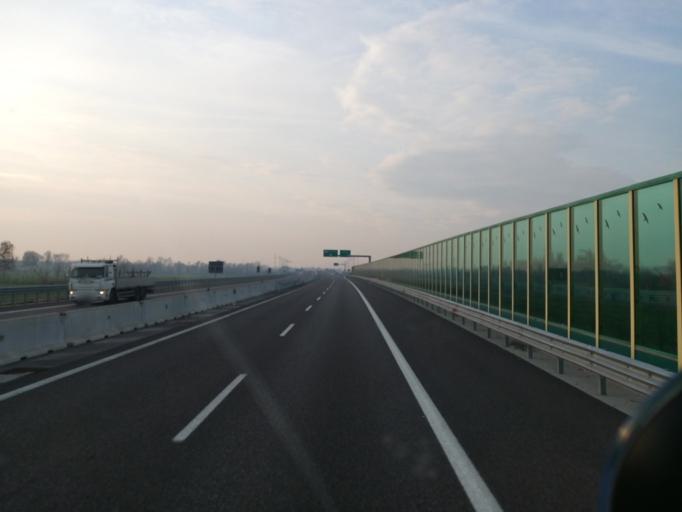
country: IT
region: Lombardy
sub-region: Provincia di Brescia
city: Flero
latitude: 45.4767
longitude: 10.1674
